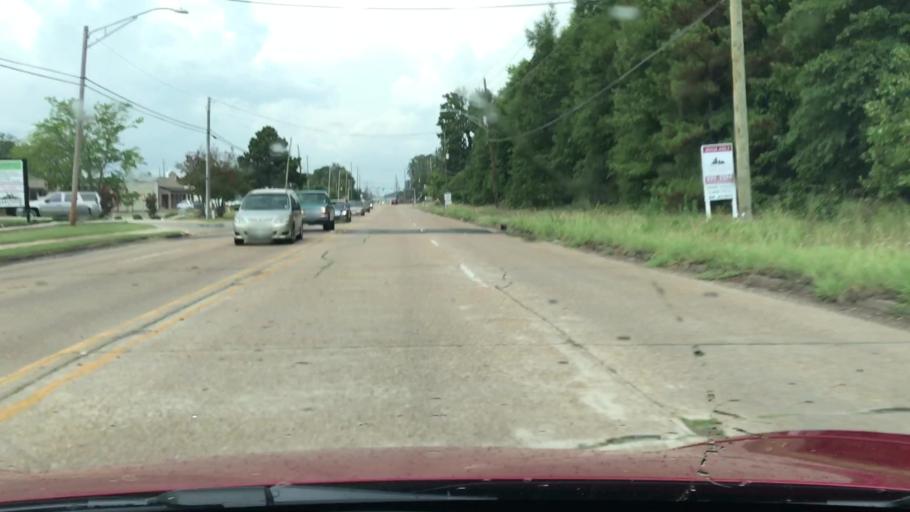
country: US
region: Louisiana
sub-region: Bossier Parish
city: Bossier City
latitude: 32.4099
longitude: -93.7632
